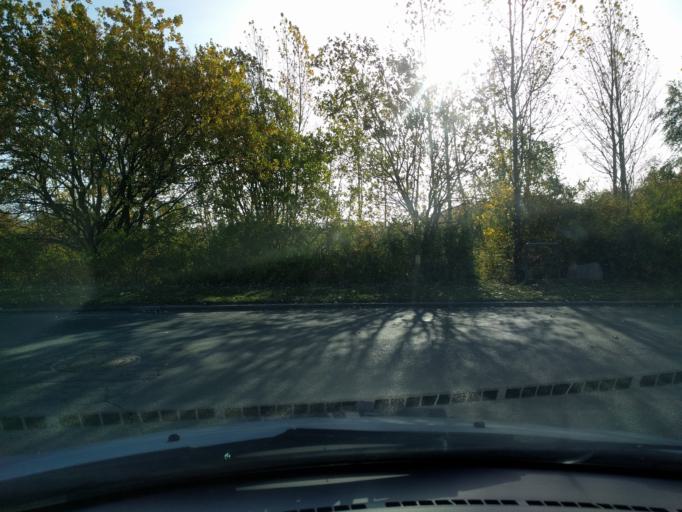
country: DK
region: South Denmark
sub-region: Kerteminde Kommune
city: Munkebo
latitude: 55.4565
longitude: 10.5403
